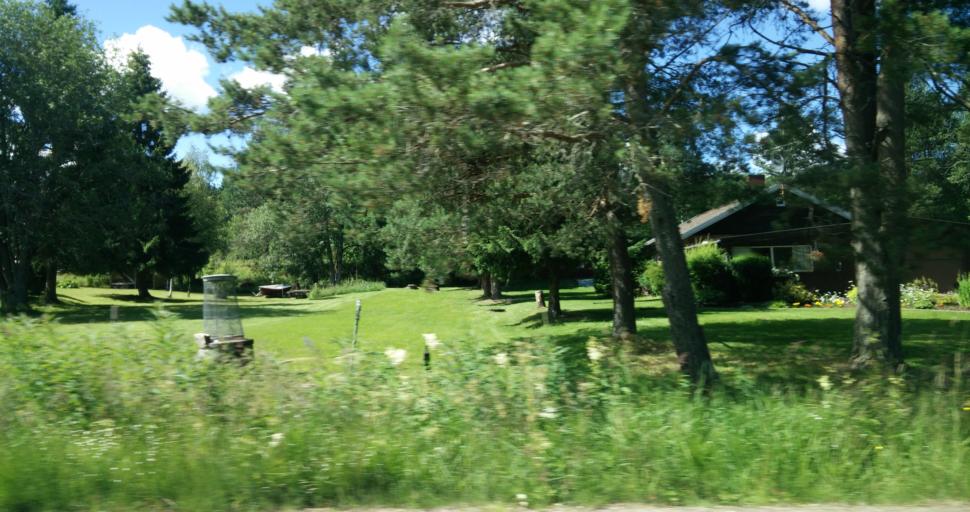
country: SE
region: Vaermland
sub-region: Hagfors Kommun
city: Hagfors
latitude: 60.0302
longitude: 13.6253
